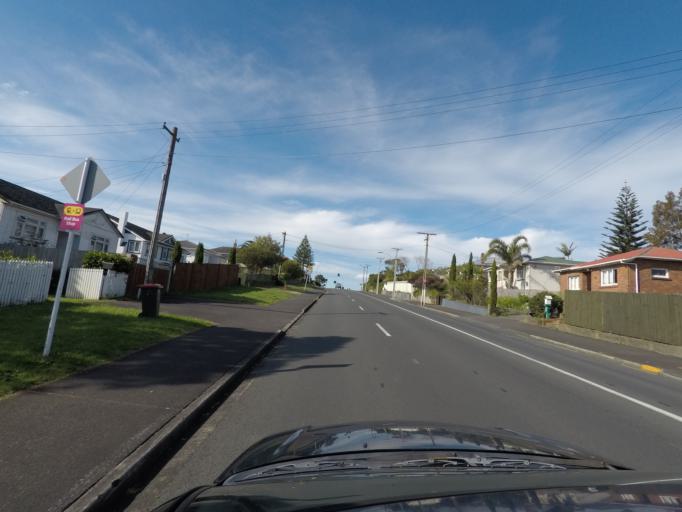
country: NZ
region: Auckland
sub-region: Auckland
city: Rosebank
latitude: -36.8978
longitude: 174.6998
